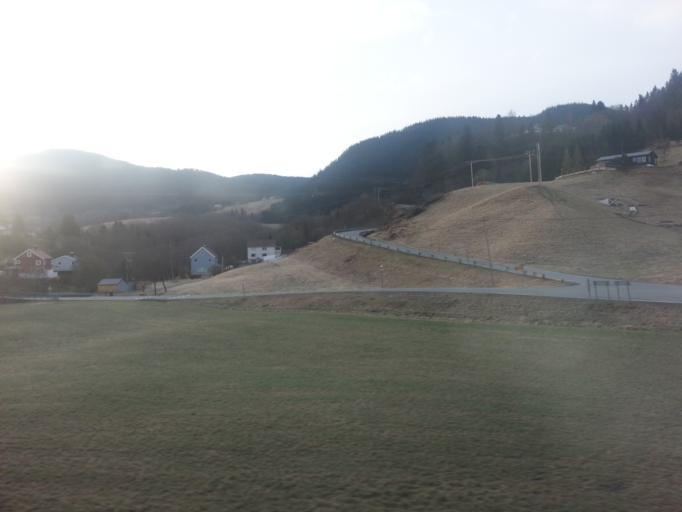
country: NO
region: Sor-Trondelag
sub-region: Melhus
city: Melhus
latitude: 63.3046
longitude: 10.3339
